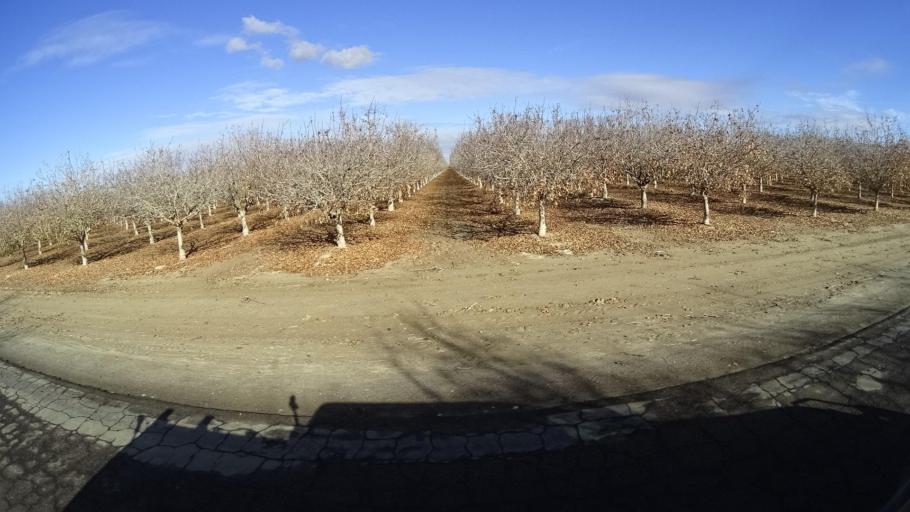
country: US
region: California
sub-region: Kern County
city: Shafter
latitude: 35.3836
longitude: -119.2679
